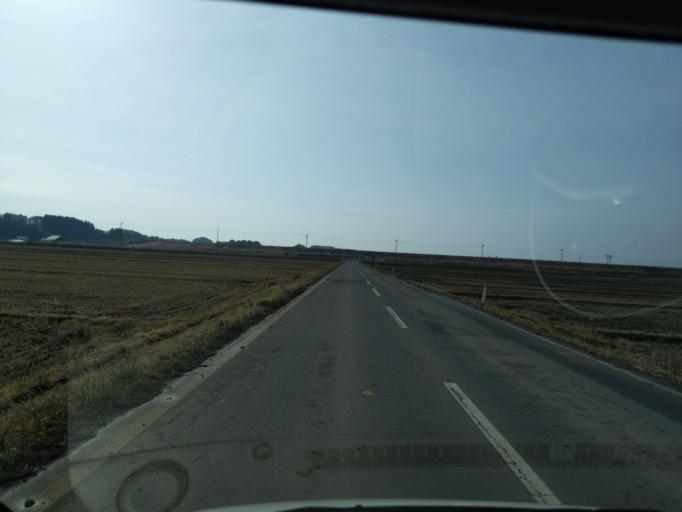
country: JP
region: Miyagi
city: Wakuya
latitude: 38.7124
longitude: 141.1553
